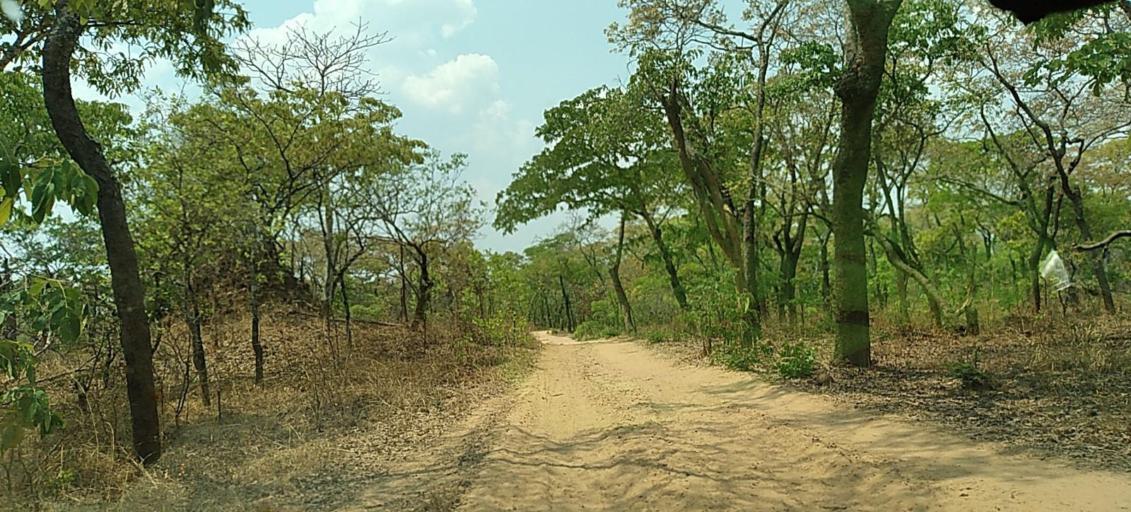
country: ZM
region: North-Western
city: Kabompo
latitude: -13.6388
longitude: 24.3838
